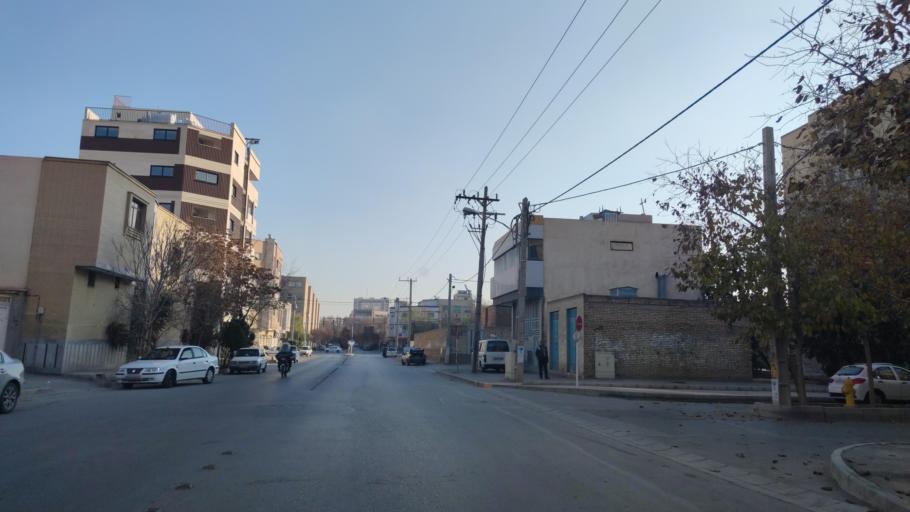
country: IR
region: Isfahan
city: Isfahan
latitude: 32.7106
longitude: 51.6854
